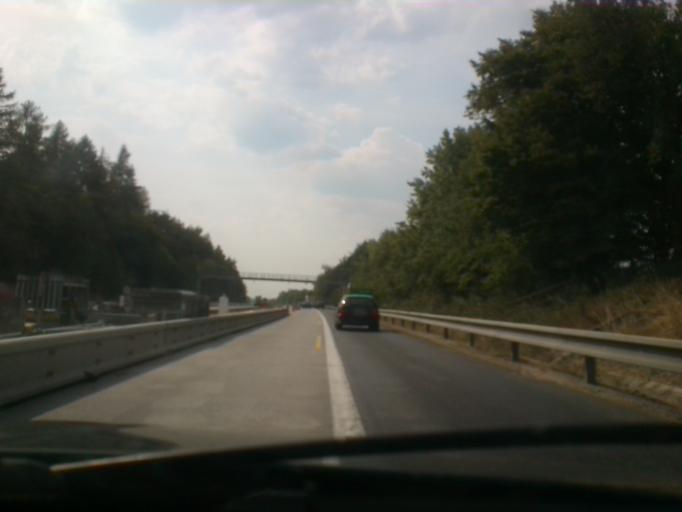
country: CZ
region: Central Bohemia
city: Divisov
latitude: 49.8393
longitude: 14.8263
